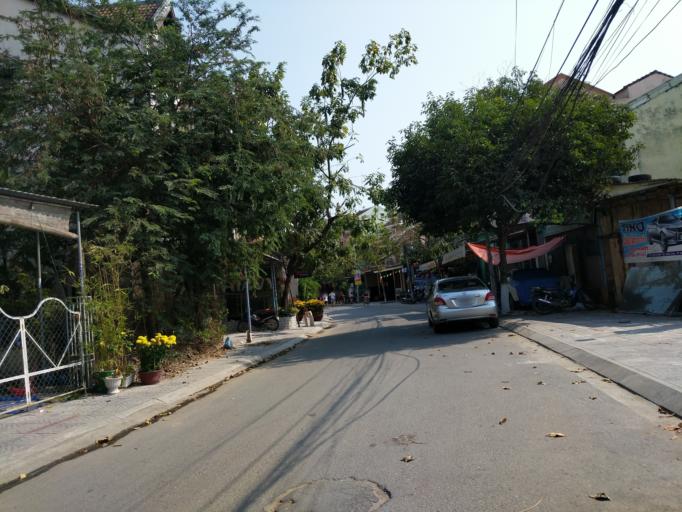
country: VN
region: Quang Nam
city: Hoi An
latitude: 15.8827
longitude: 108.3244
